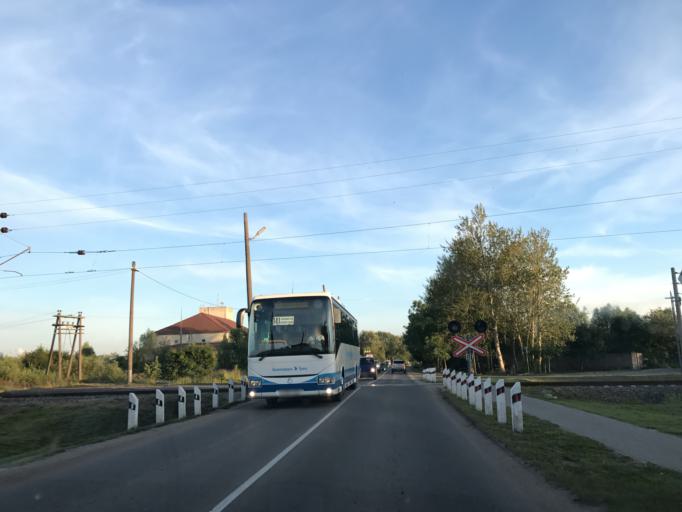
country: RU
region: Kaliningrad
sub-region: Zelenogradskiy Rayon
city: Zelenogradsk
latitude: 54.9527
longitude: 20.4705
